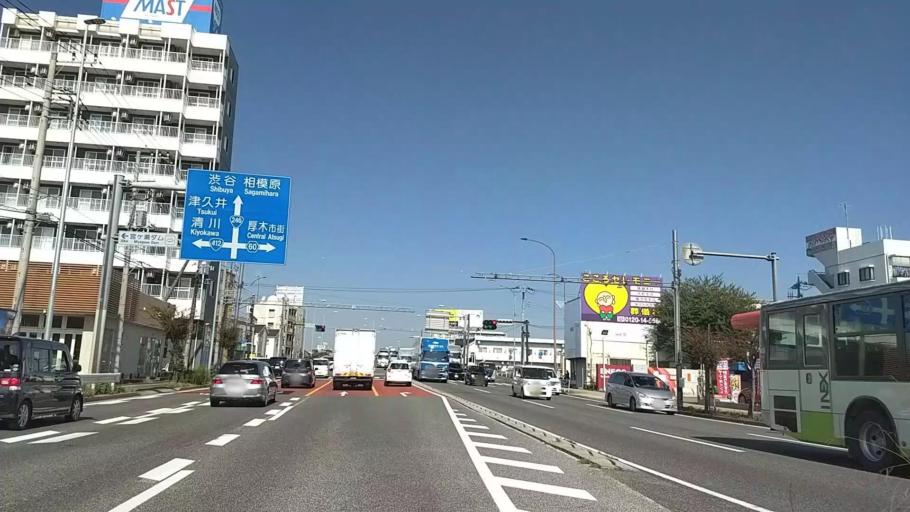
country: JP
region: Kanagawa
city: Atsugi
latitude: 35.4491
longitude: 139.3584
